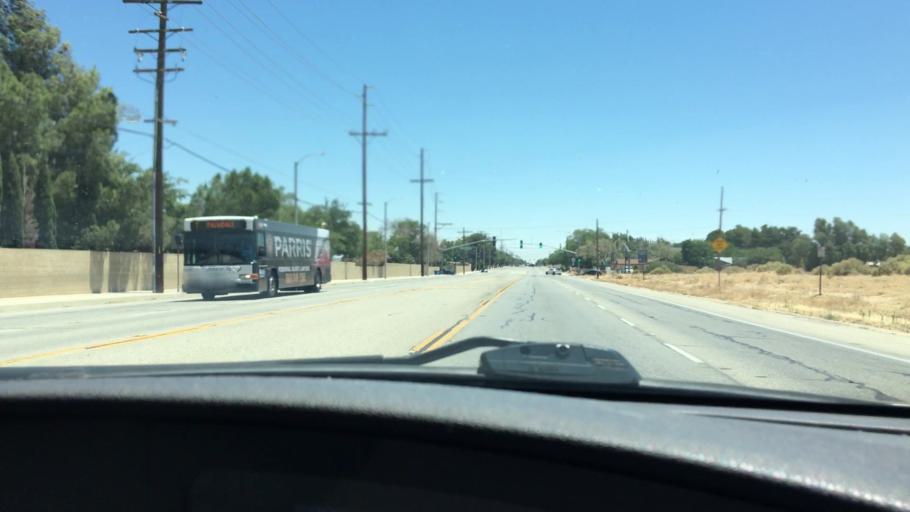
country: US
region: California
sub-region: Los Angeles County
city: Quartz Hill
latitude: 34.6602
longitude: -118.1945
